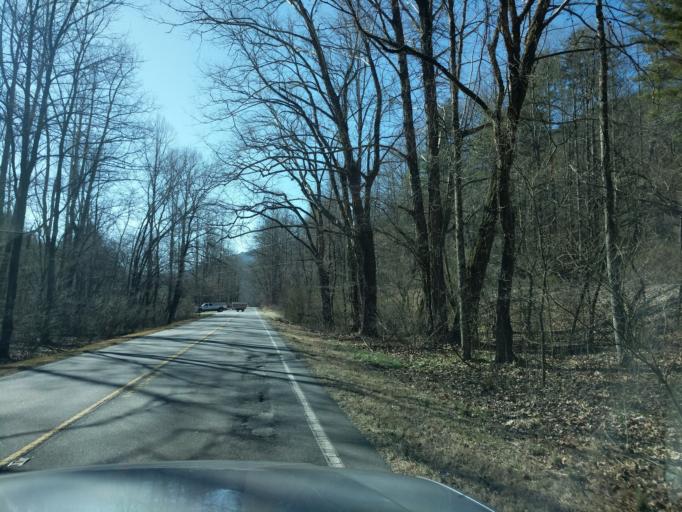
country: US
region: North Carolina
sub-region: Graham County
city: Robbinsville
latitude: 35.2844
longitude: -83.6712
